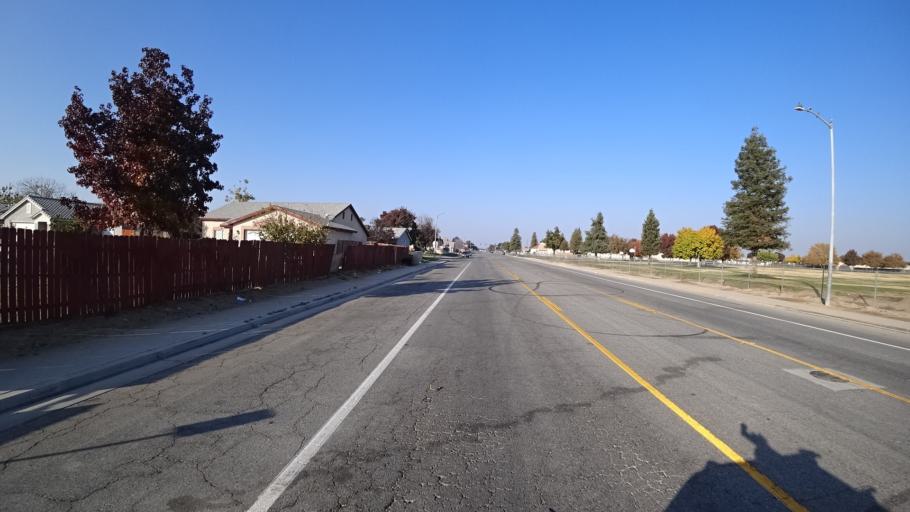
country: US
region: California
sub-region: Kern County
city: Greenfield
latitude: 35.2855
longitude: -119.0119
